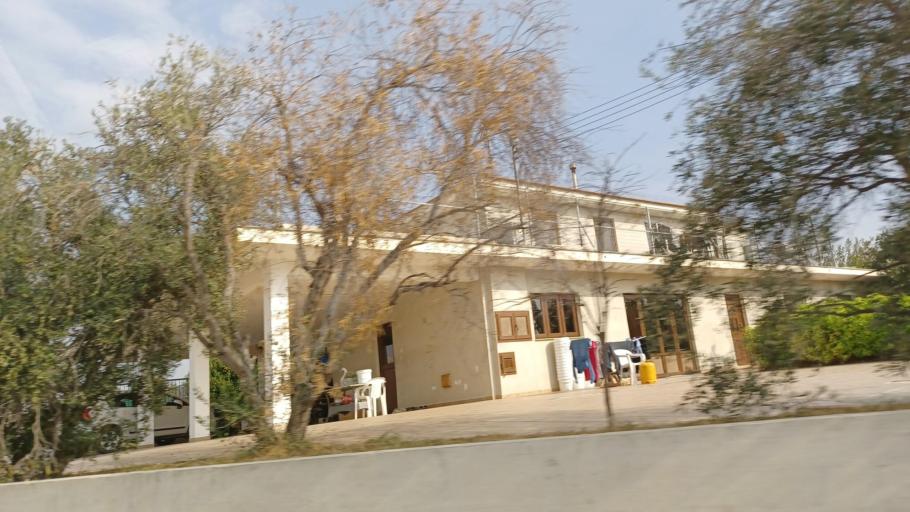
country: CY
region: Larnaka
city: Troulloi
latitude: 35.0046
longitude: 33.5724
